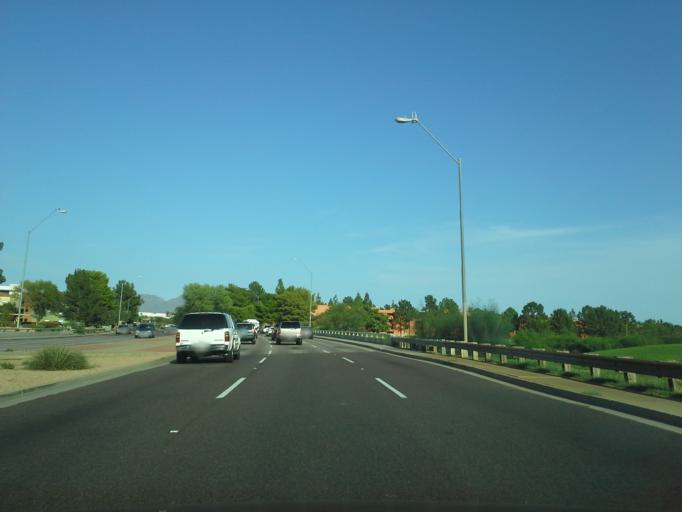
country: US
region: Arizona
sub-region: Maricopa County
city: Paradise Valley
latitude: 33.5972
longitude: -111.9936
